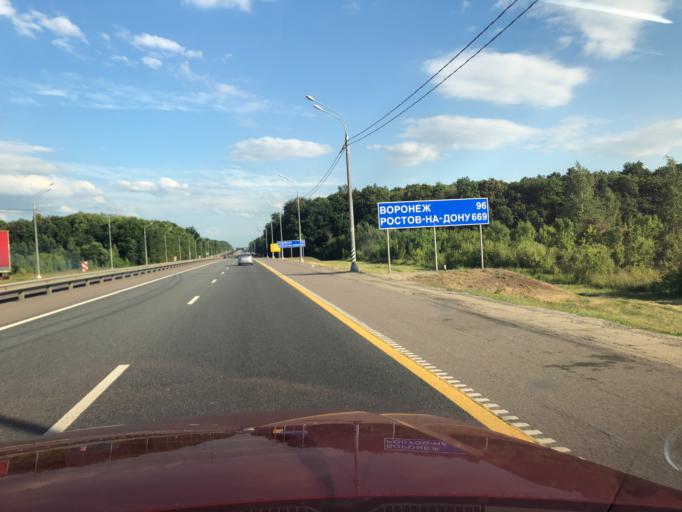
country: RU
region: Lipetsk
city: Zadonsk
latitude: 52.4222
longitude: 38.8342
